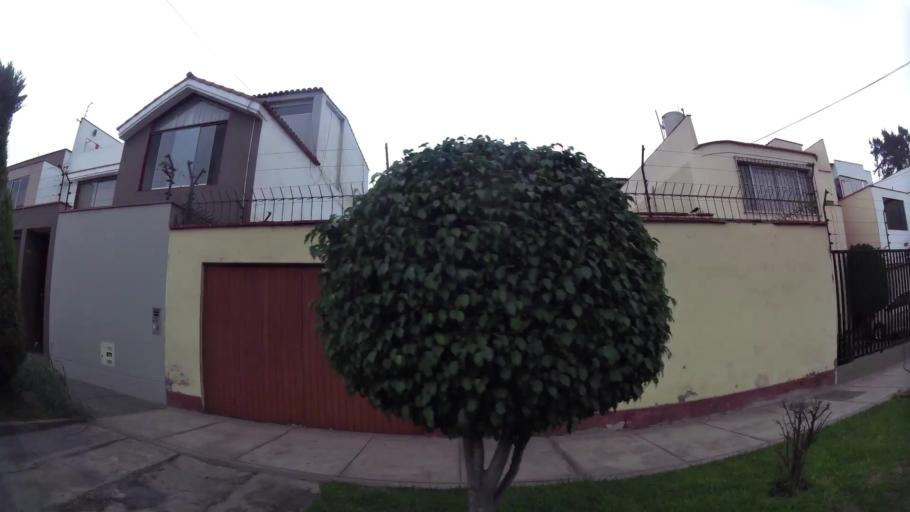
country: PE
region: Lima
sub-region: Lima
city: Surco
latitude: -12.1227
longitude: -76.9874
